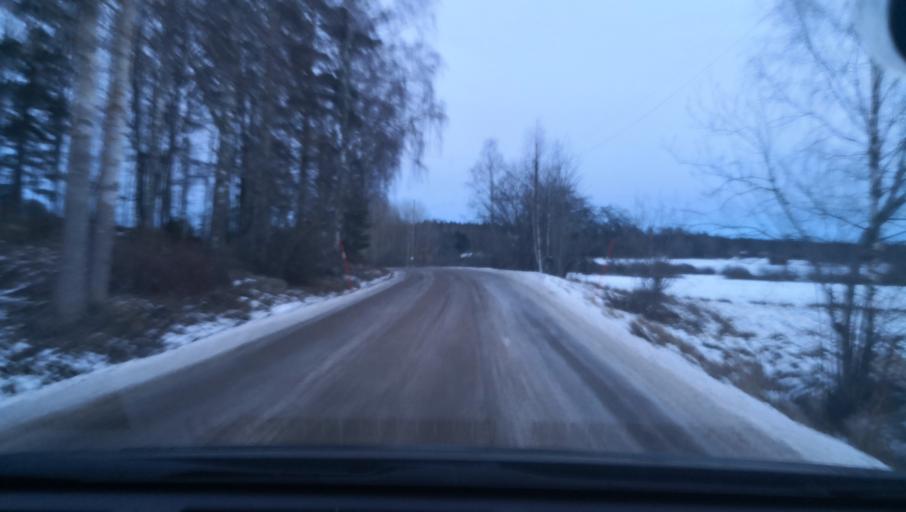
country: SE
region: Dalarna
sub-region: Avesta Kommun
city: Horndal
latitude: 60.2005
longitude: 16.5026
